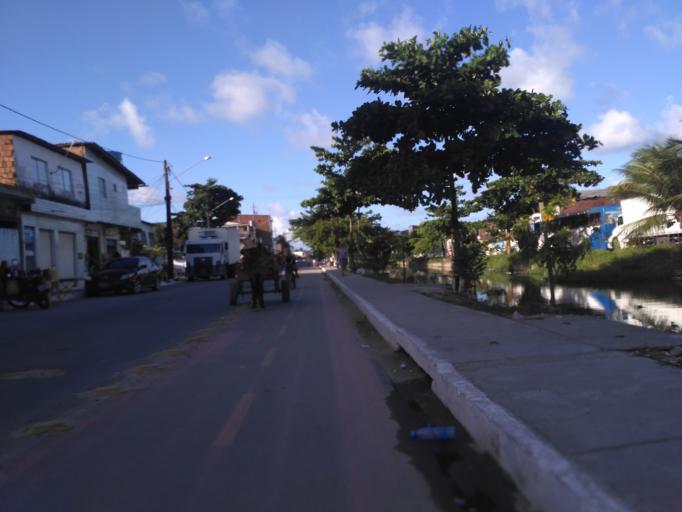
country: BR
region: Pernambuco
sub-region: Jaboatao Dos Guararapes
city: Jaboatao
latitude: -8.1811
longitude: -34.9341
